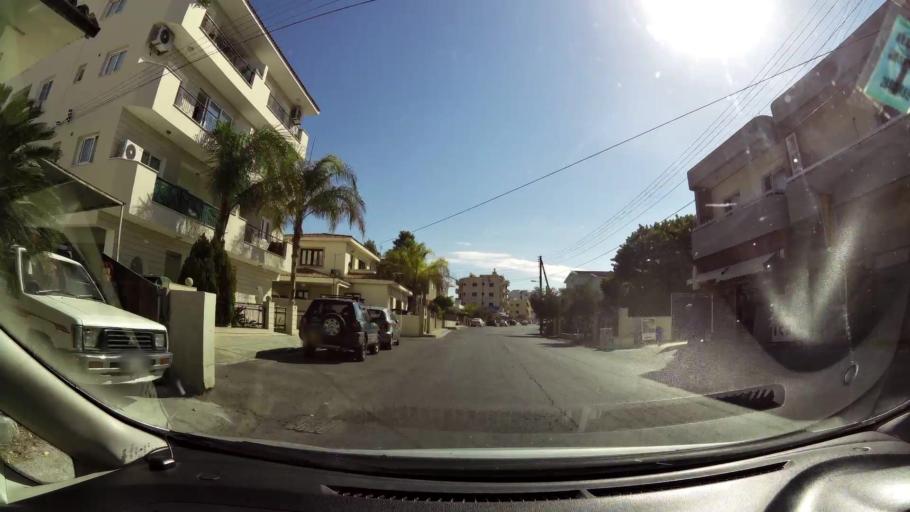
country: CY
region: Lefkosia
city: Nicosia
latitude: 35.1406
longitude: 33.3429
